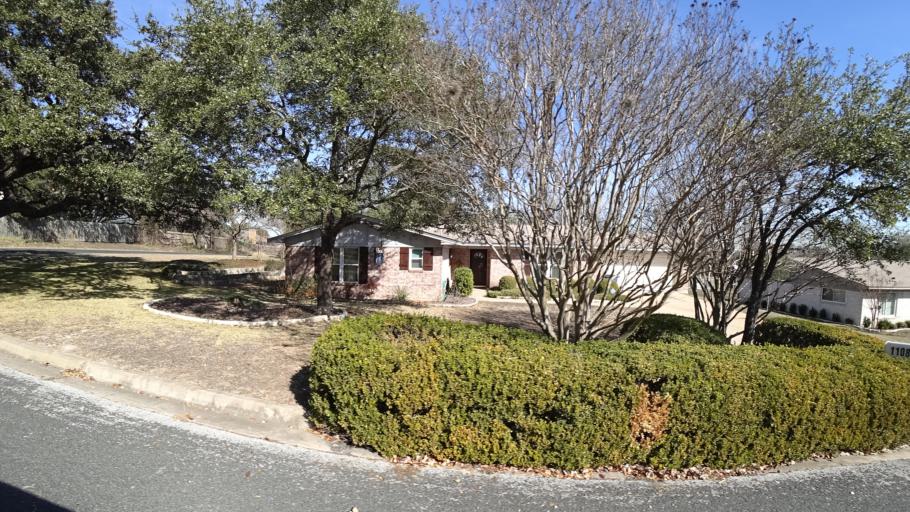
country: US
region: Texas
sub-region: Travis County
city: Wells Branch
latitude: 30.3883
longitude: -97.6904
